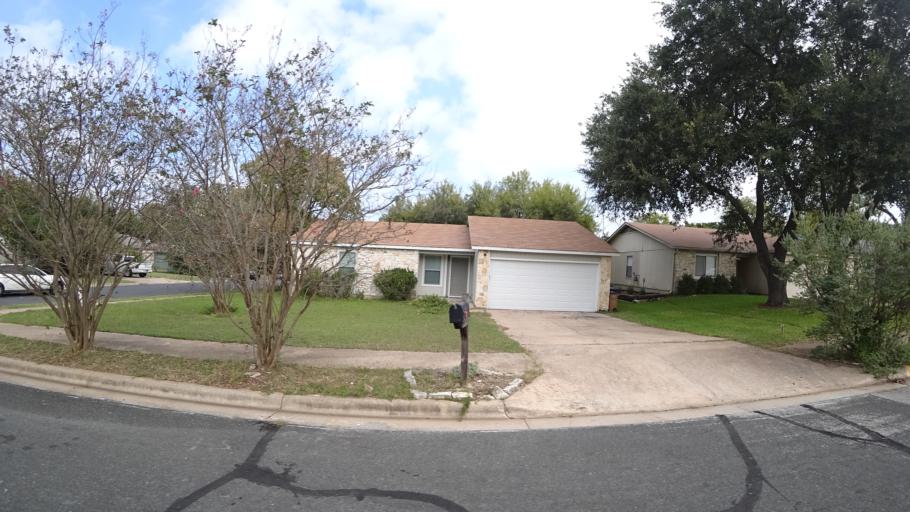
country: US
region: Texas
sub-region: Travis County
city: Shady Hollow
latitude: 30.2023
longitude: -97.8315
